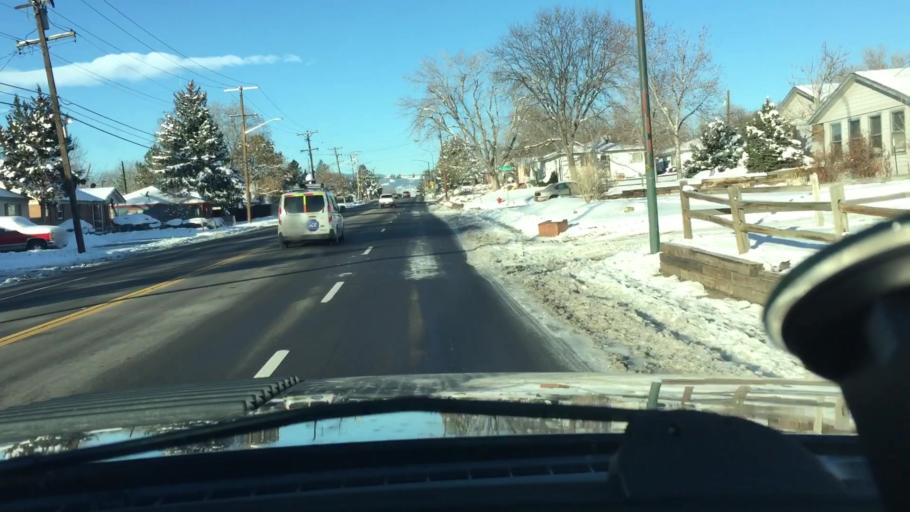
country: US
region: Colorado
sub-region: Adams County
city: Westminster
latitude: 39.8419
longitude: -105.0312
